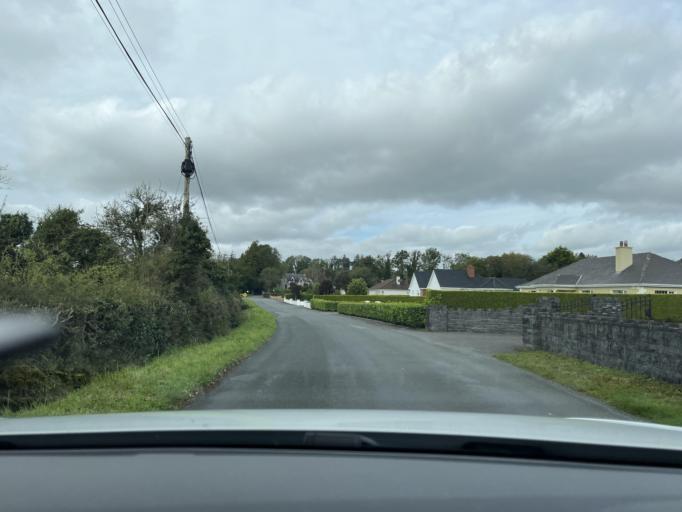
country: IE
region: Connaught
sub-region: County Leitrim
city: Carrick-on-Shannon
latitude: 53.9653
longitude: -8.0872
